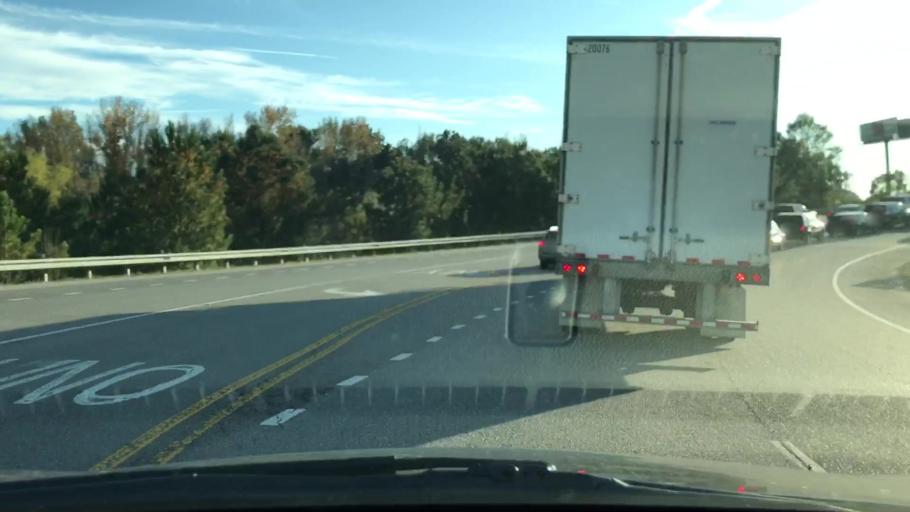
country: US
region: Alabama
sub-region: Calhoun County
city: Oxford
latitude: 33.6141
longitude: -85.7849
